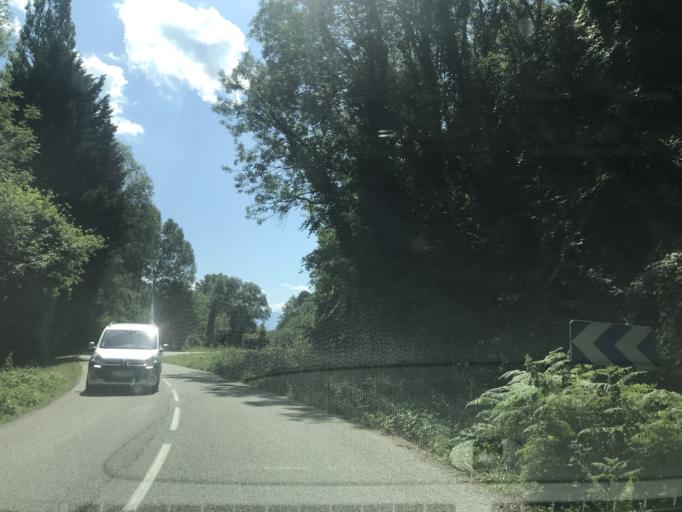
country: FR
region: Rhone-Alpes
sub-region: Departement de la Savoie
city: Chatillon
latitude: 45.8095
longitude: 5.8151
